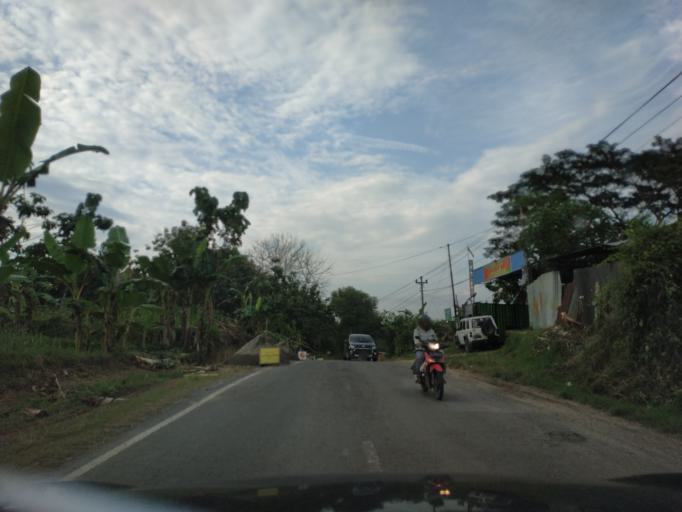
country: ID
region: Central Java
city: Medang
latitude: -6.9081
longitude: 111.4404
